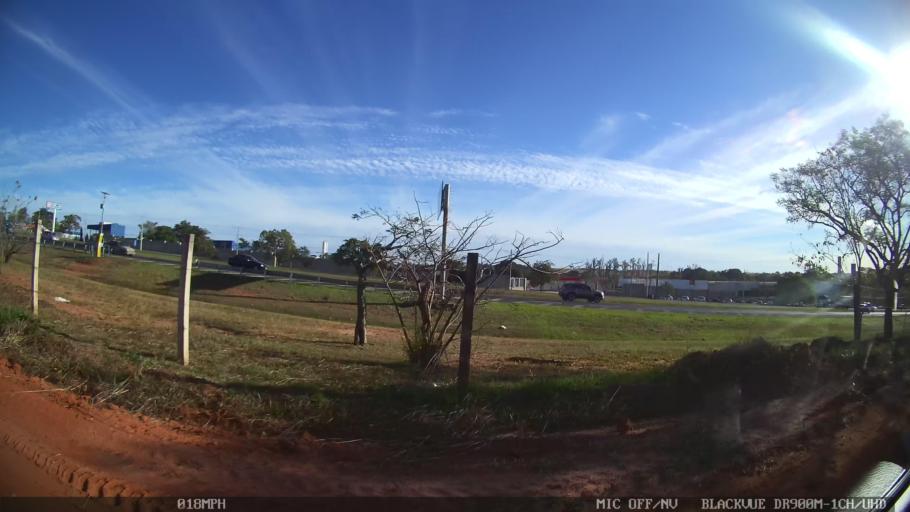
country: BR
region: Sao Paulo
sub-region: Sao Jose Do Rio Preto
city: Sao Jose do Rio Preto
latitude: -20.8741
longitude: -49.3224
